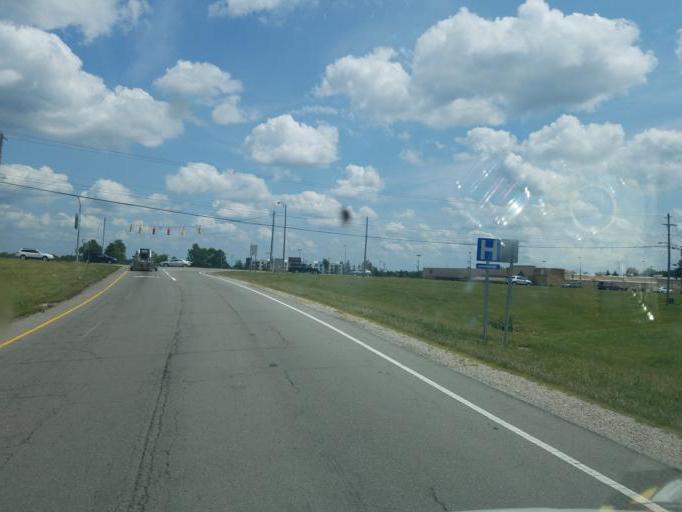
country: US
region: Ohio
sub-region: Richland County
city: Ontario
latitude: 40.7835
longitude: -82.5911
